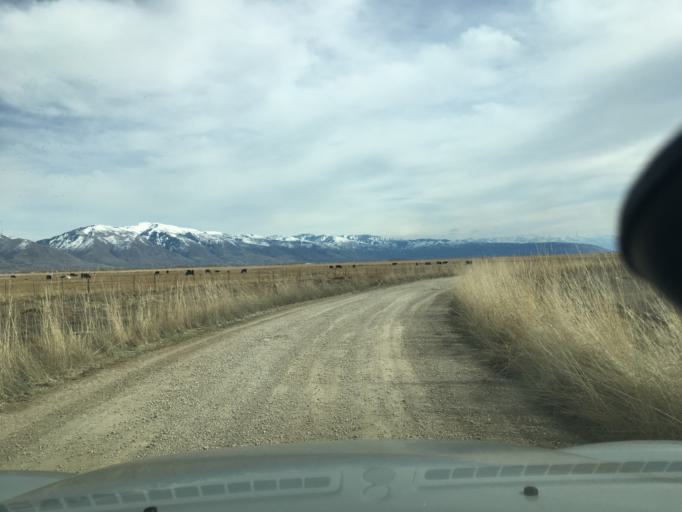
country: US
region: Utah
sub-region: Davis County
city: Layton
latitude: 41.0430
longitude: -112.0263
